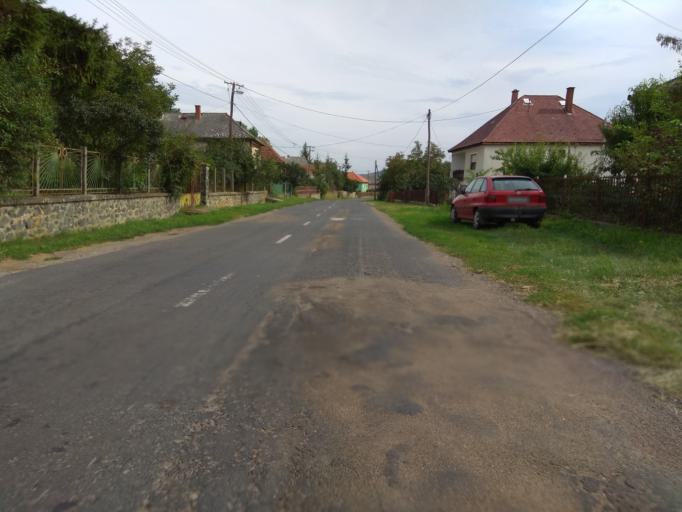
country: HU
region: Heves
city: Tarnalelesz
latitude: 48.0304
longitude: 20.2560
